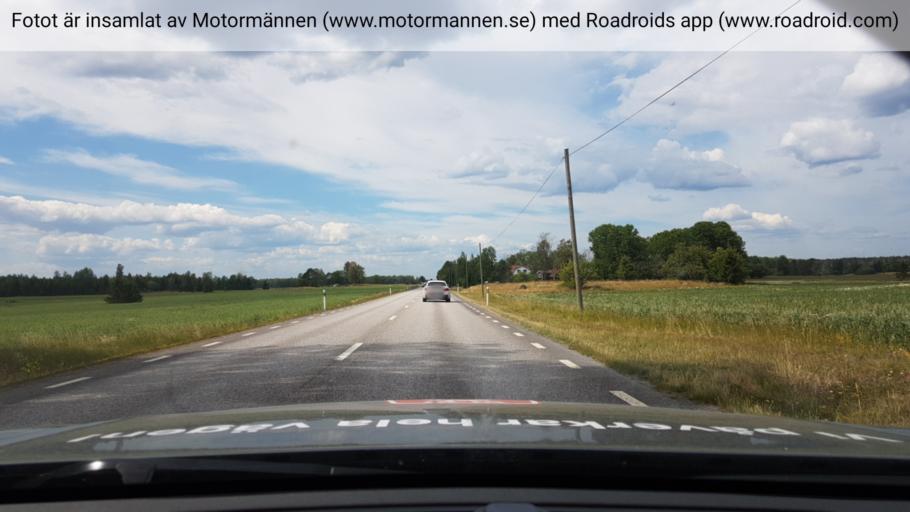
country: SE
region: Vaestmanland
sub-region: Sala Kommun
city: Sala
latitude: 59.8402
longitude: 16.6786
